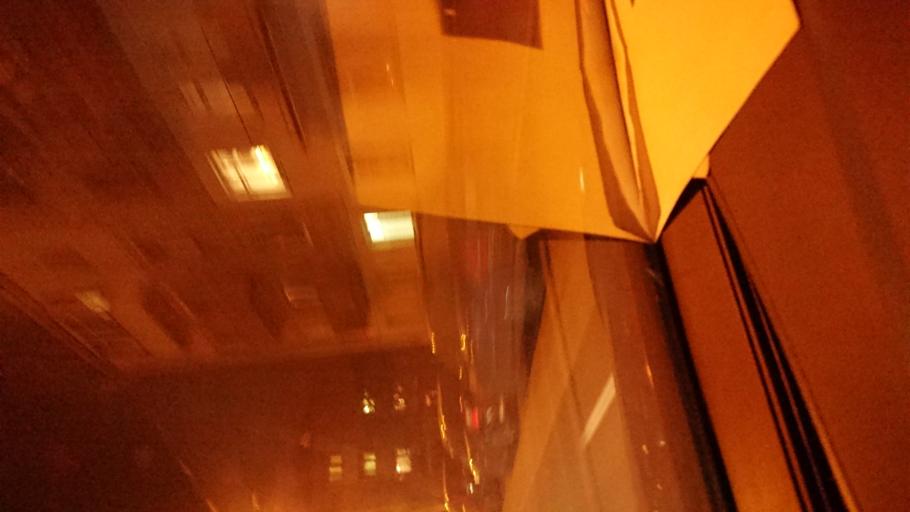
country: BY
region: Minsk
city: Minsk
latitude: 53.9297
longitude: 27.6008
